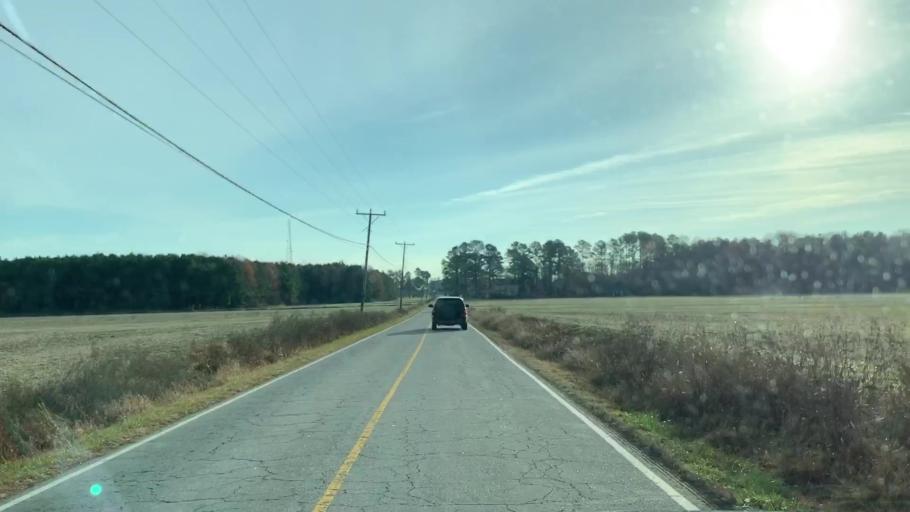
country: US
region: Virginia
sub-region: City of Virginia Beach
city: Virginia Beach
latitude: 36.6942
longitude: -76.0229
